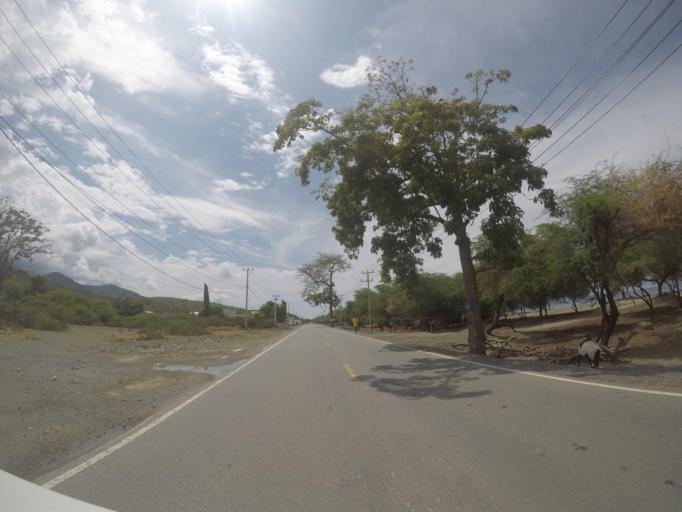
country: TL
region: Liquica
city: Liquica
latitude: -8.5647
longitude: 125.4018
